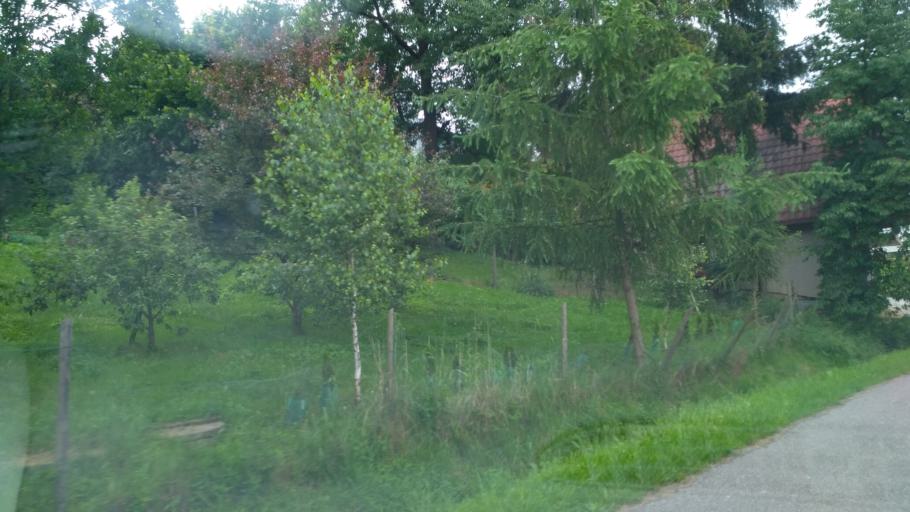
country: PL
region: Subcarpathian Voivodeship
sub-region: Powiat przemyski
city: Nienadowa
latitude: 49.8617
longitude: 22.4093
